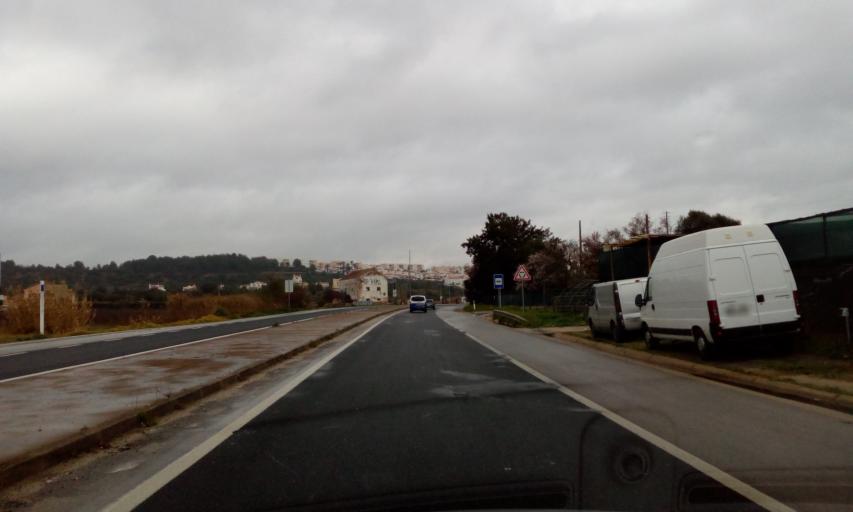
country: PT
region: Faro
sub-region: Lagos
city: Lagos
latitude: 37.1222
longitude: -8.6731
